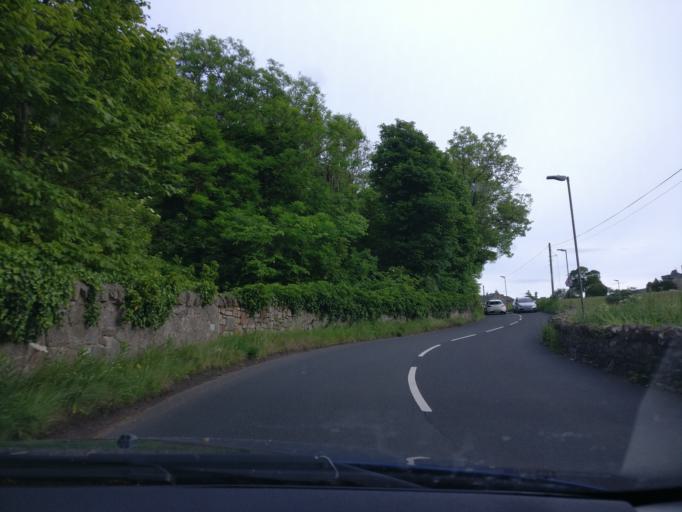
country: GB
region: Scotland
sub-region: West Lothian
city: Seafield
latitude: 55.9281
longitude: -3.1384
